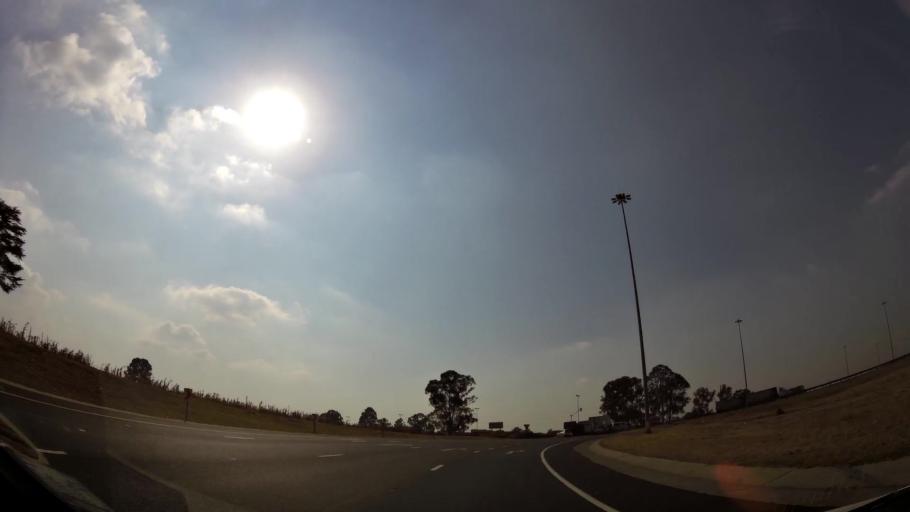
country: ZA
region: Gauteng
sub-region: Ekurhuleni Metropolitan Municipality
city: Brakpan
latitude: -26.1657
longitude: 28.3965
